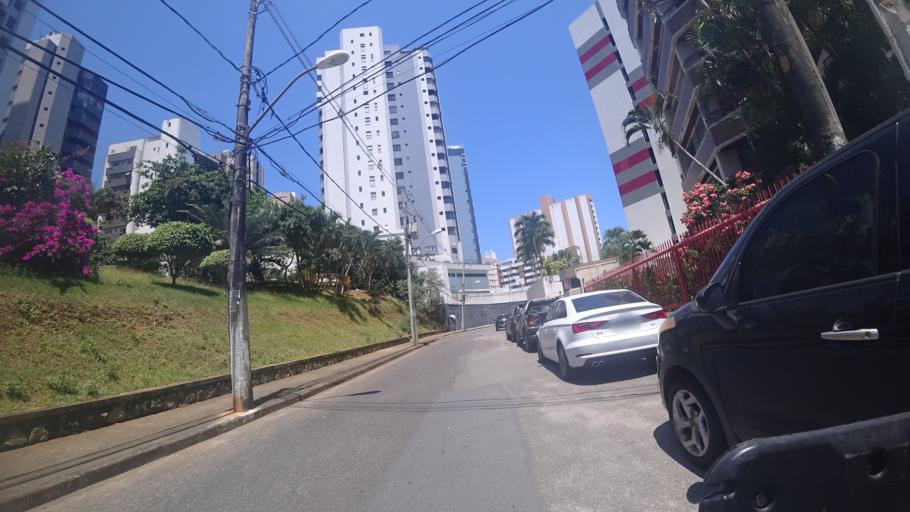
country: BR
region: Bahia
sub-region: Salvador
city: Salvador
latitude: -12.9867
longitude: -38.4629
